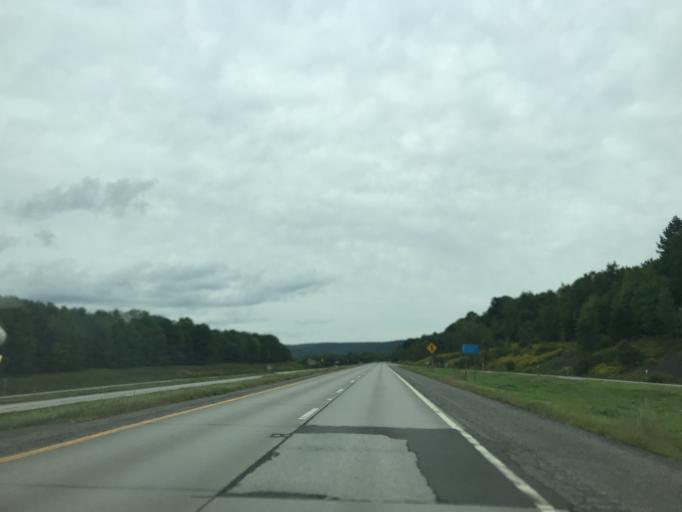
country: US
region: New York
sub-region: Otsego County
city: Oneonta
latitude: 42.4829
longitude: -74.9654
